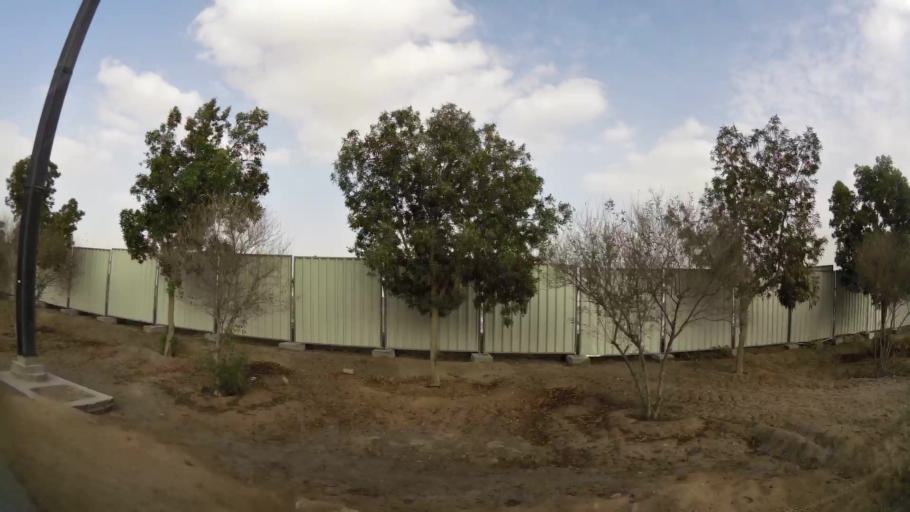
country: AE
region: Abu Dhabi
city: Abu Dhabi
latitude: 24.5034
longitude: 54.6026
